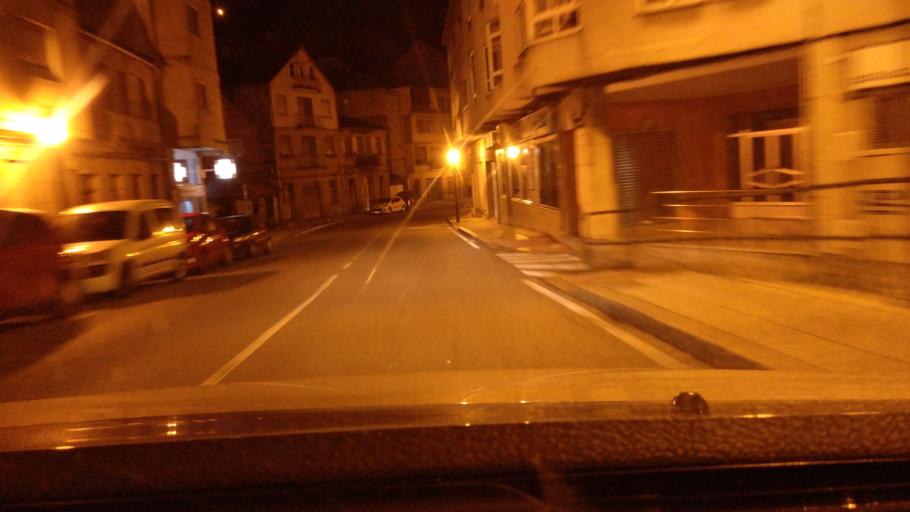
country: ES
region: Galicia
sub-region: Provincia de Pontevedra
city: Moana
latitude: 42.2794
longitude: -8.7375
